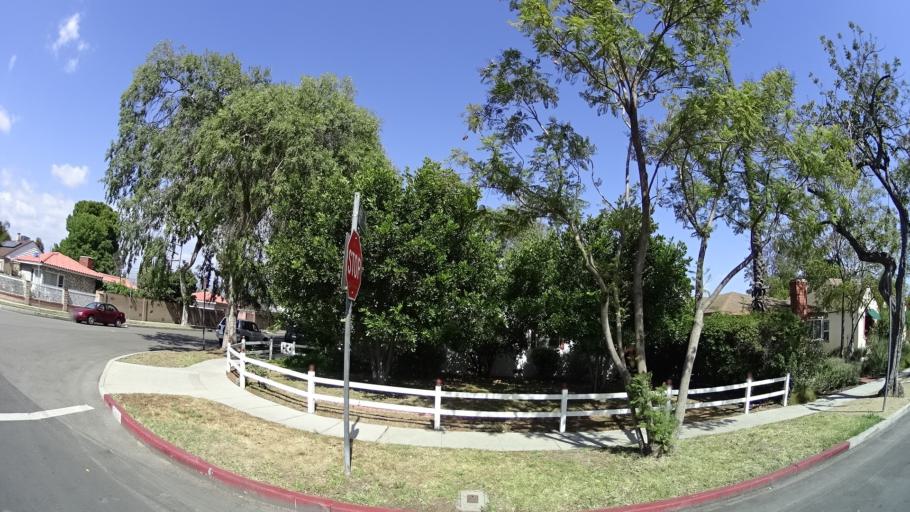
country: US
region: California
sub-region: Los Angeles County
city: North Hollywood
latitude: 34.1774
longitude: -118.3867
